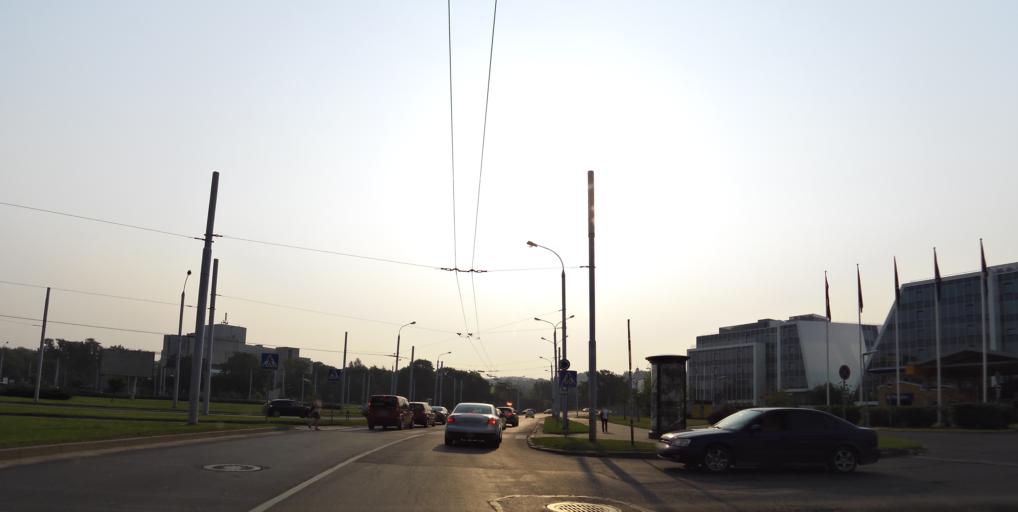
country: LT
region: Vilnius County
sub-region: Vilnius
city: Vilnius
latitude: 54.6956
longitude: 25.2972
